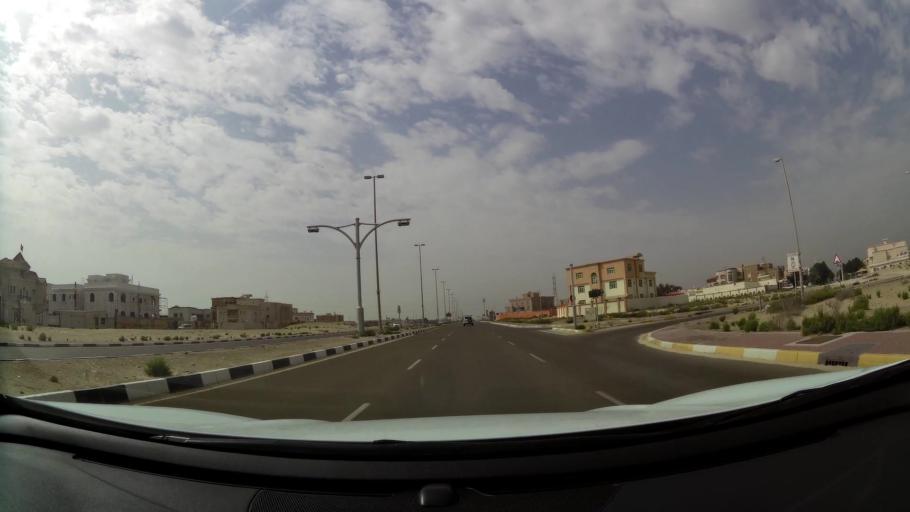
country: AE
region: Abu Dhabi
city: Abu Dhabi
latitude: 24.3134
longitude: 54.6453
